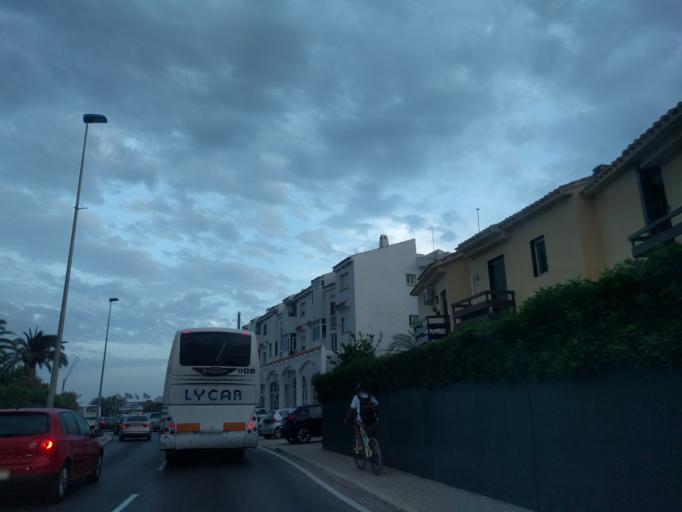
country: ES
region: Murcia
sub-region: Murcia
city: La Manga del Mar Menor
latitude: 37.6624
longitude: -0.7292
